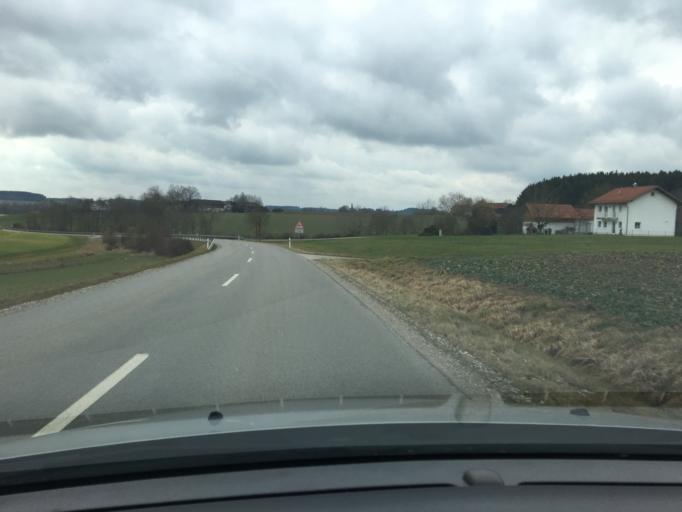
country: DE
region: Bavaria
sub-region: Lower Bavaria
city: Gangkofen
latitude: 48.4442
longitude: 12.5851
